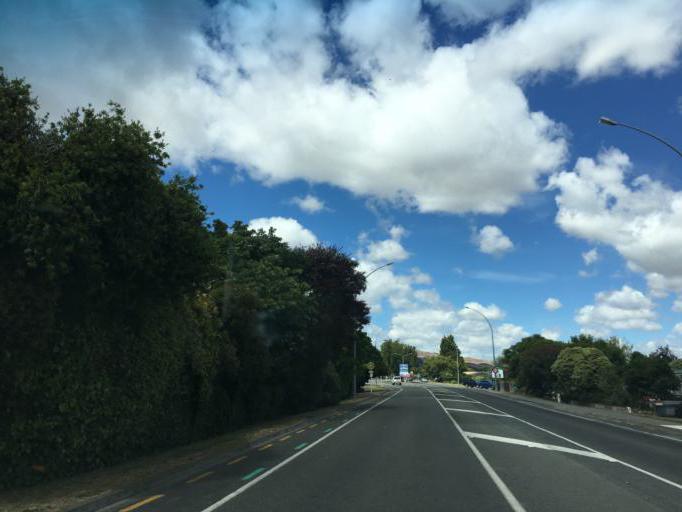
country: NZ
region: Hawke's Bay
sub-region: Hastings District
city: Hastings
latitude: -39.6603
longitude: 176.8848
